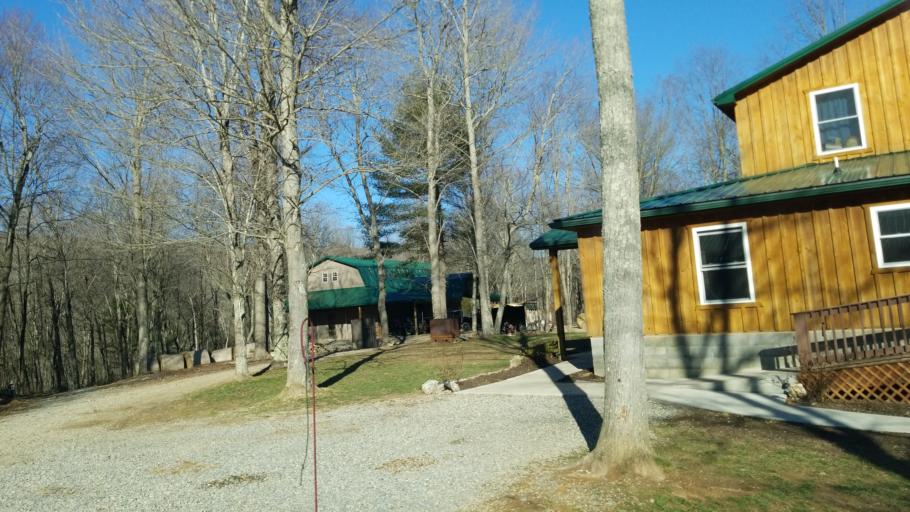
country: US
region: Virginia
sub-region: Giles County
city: Narrows
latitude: 37.1917
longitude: -80.8317
